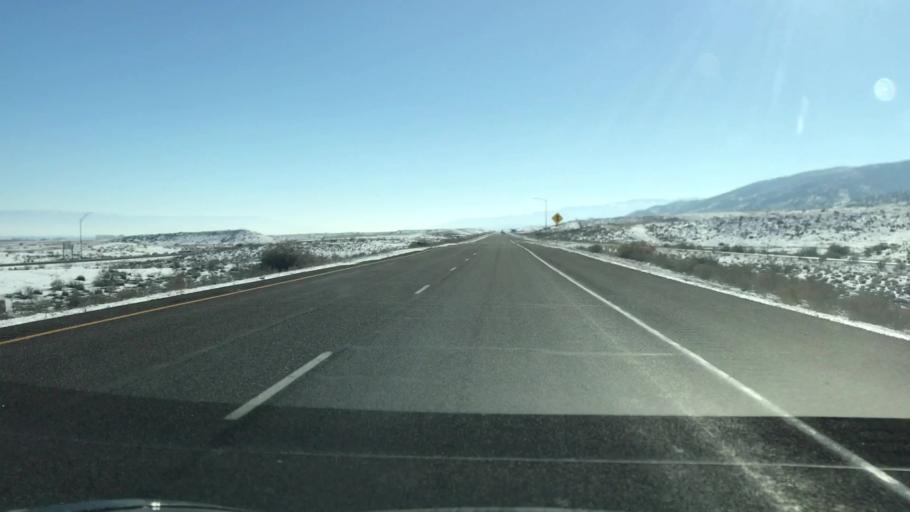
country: US
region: Colorado
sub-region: Mesa County
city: Loma
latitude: 39.2120
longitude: -108.8664
